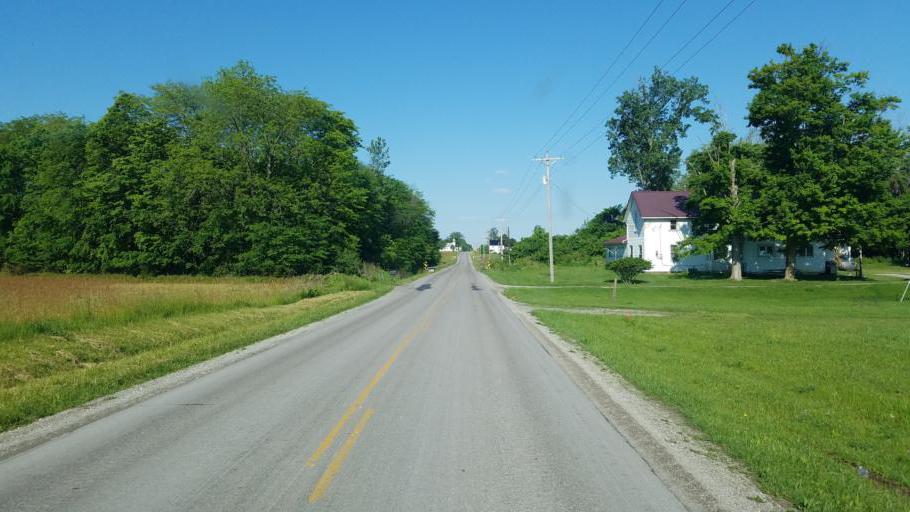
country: US
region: Ohio
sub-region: Hardin County
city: Kenton
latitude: 40.5850
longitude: -83.4961
